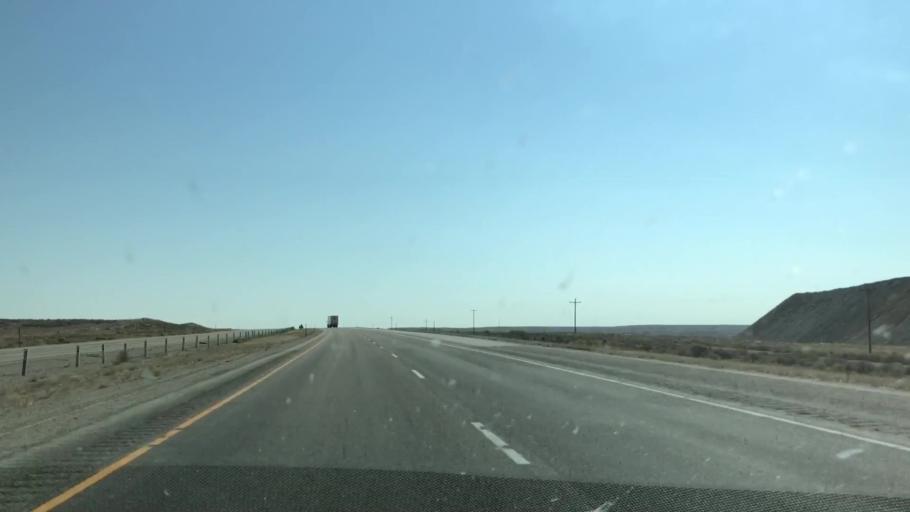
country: US
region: Wyoming
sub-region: Sweetwater County
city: Rock Springs
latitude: 41.6466
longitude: -108.6522
